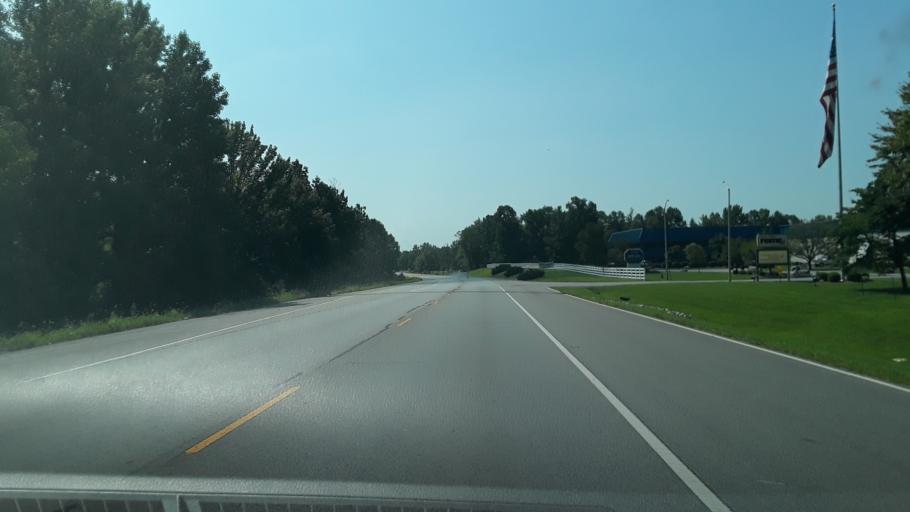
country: US
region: Indiana
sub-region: Clark County
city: Sellersburg
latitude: 38.3754
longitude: -85.7639
